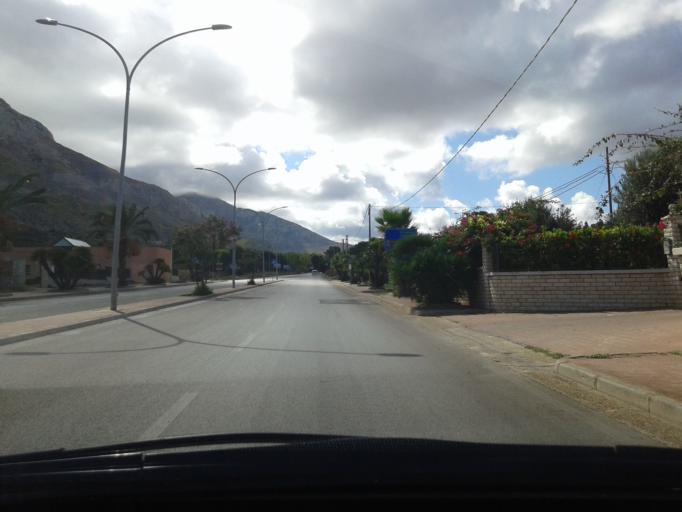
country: IT
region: Sicily
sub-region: Trapani
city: San Vito Lo Capo
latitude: 38.1607
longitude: 12.7369
